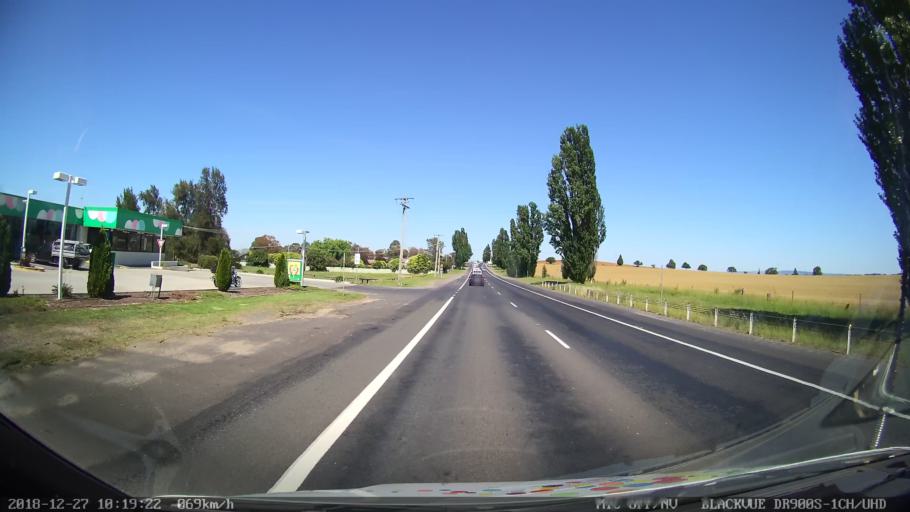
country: AU
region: New South Wales
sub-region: Bathurst Regional
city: Kelso
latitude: -33.4224
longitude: 149.6490
